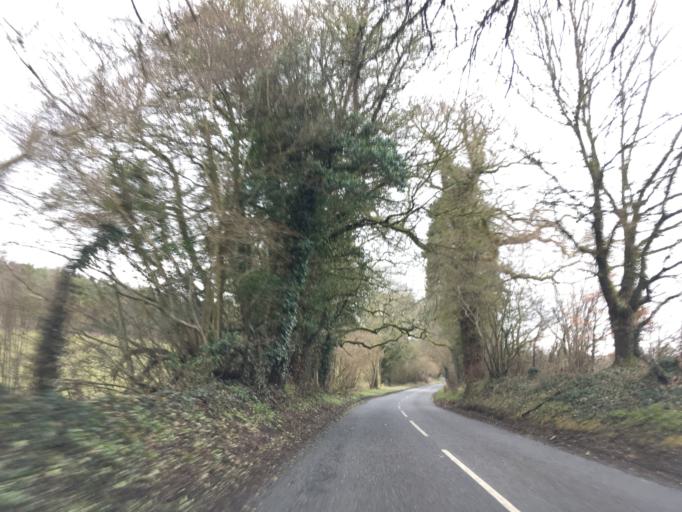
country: GB
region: England
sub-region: Wiltshire
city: Chilton Foliat
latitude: 51.4592
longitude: -1.5264
